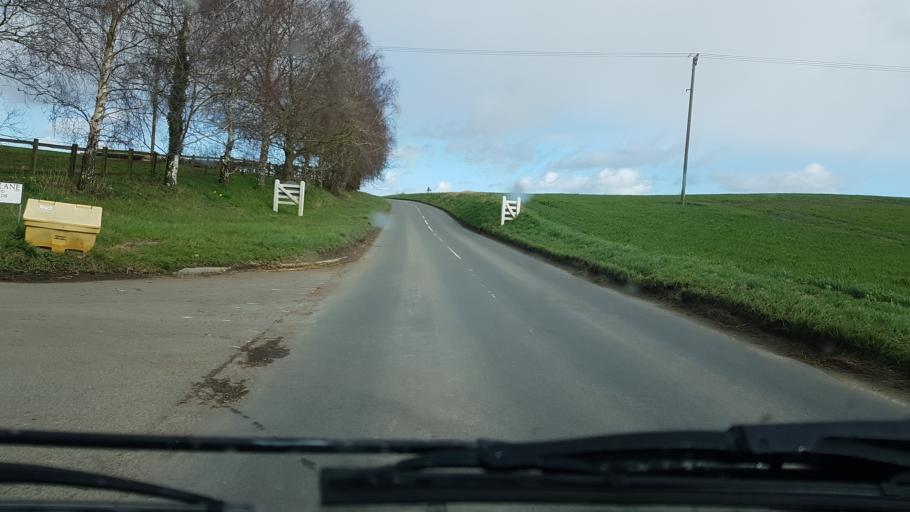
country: GB
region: England
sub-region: Wiltshire
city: Market Lavington
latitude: 51.3125
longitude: -1.9364
